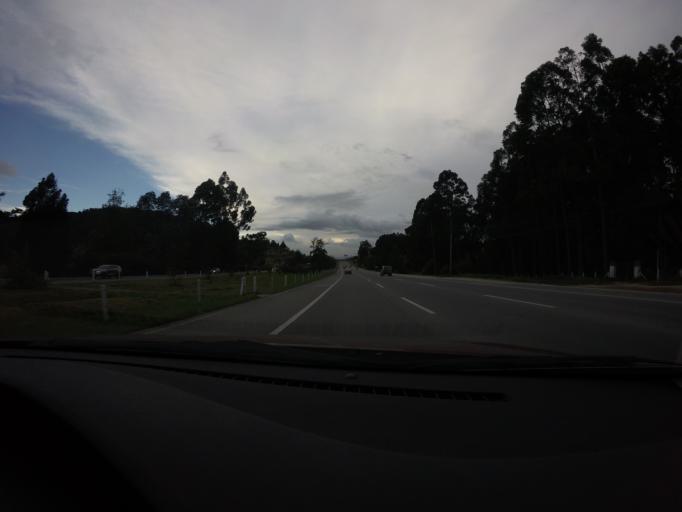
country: CO
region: Cundinamarca
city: Cajica
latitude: 4.9378
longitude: -73.9809
